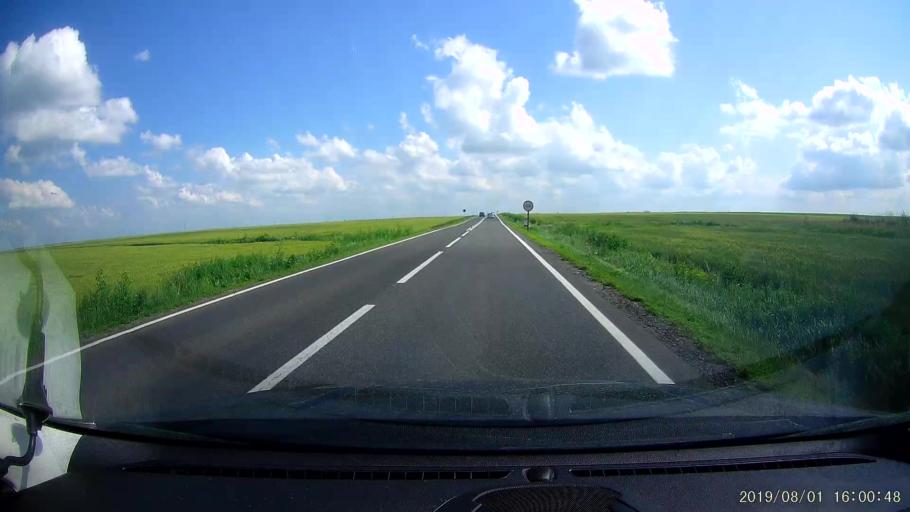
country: RO
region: Ialomita
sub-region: Comuna Ciulnita
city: Ciulnita
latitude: 44.5203
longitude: 27.3894
